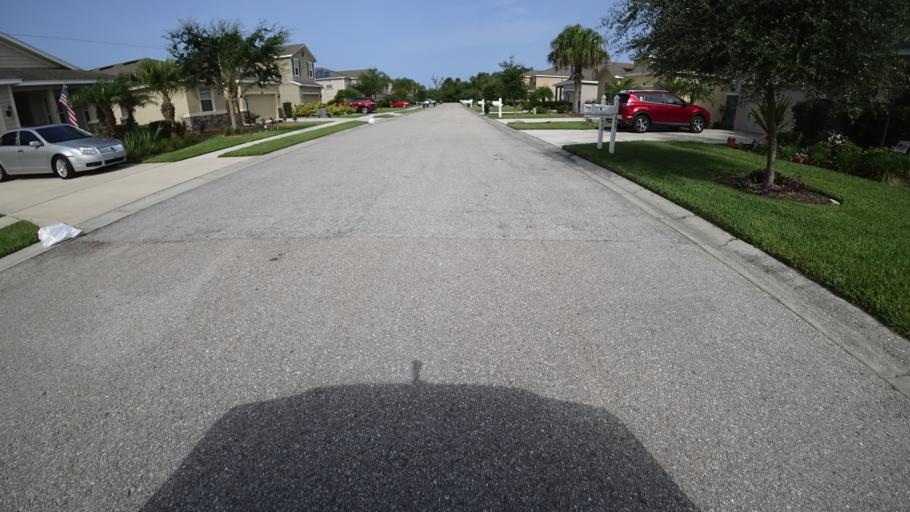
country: US
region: Florida
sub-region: Manatee County
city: Ellenton
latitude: 27.5528
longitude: -82.5054
